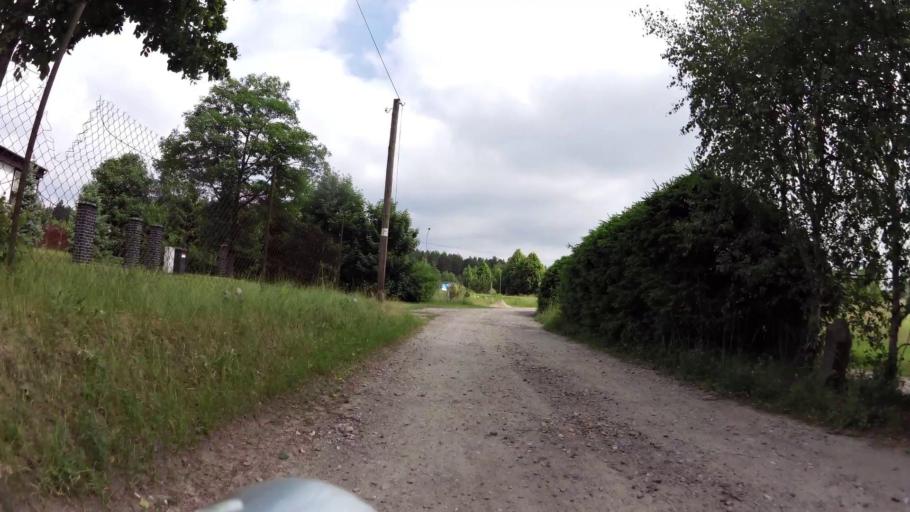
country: PL
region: West Pomeranian Voivodeship
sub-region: Powiat szczecinecki
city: Bialy Bor
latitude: 53.8972
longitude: 16.8265
